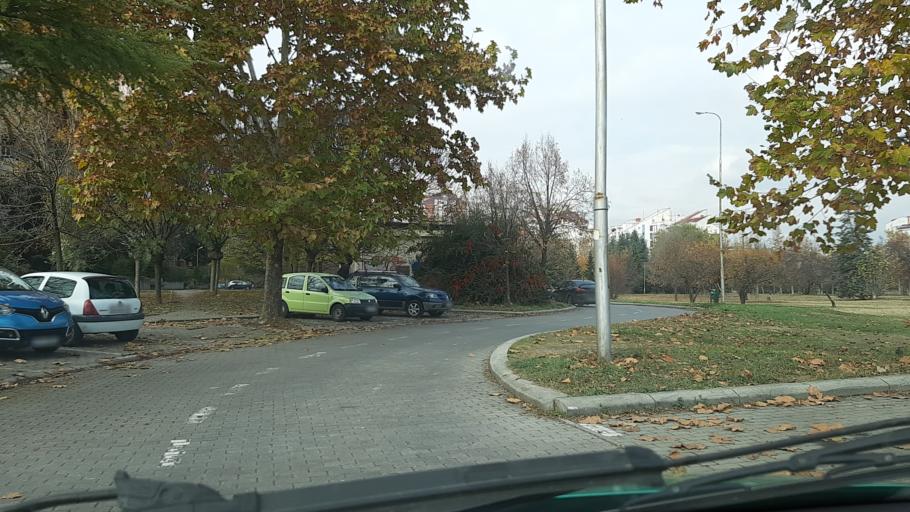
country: MK
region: Kisela Voda
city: Usje
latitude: 41.9863
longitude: 21.4710
